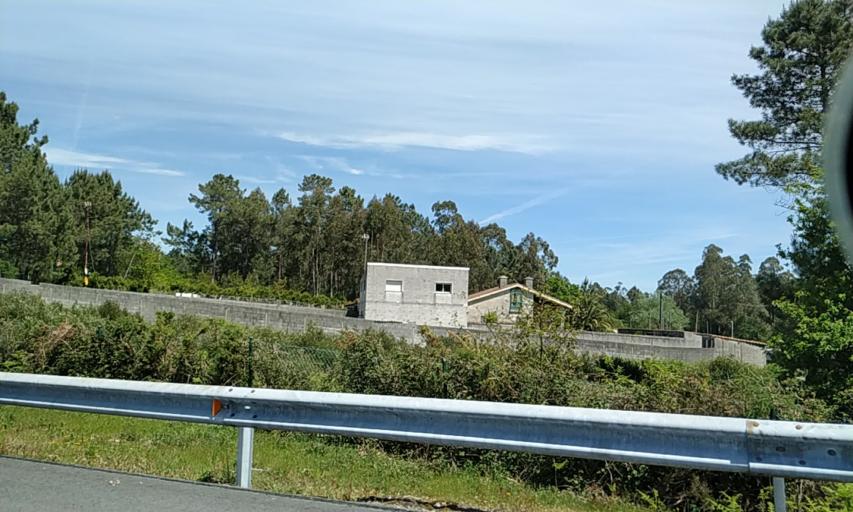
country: ES
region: Galicia
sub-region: Provincia da Coruna
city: Santiago de Compostela
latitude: 42.8099
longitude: -8.5857
